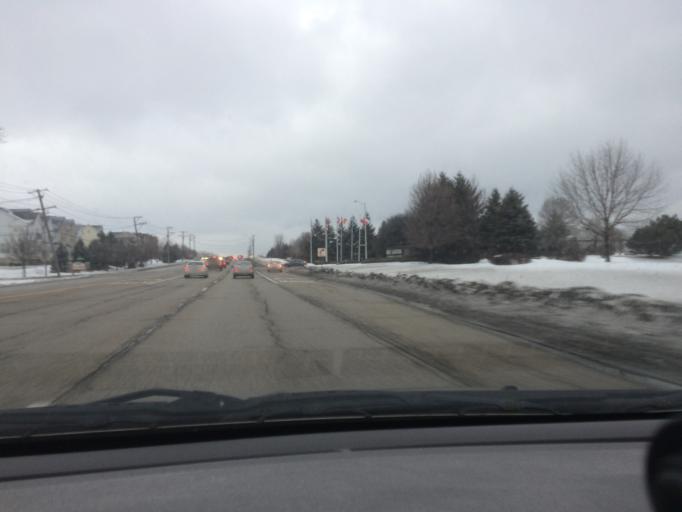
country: US
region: Illinois
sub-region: DuPage County
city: Hanover Park
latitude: 41.9741
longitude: -88.1239
